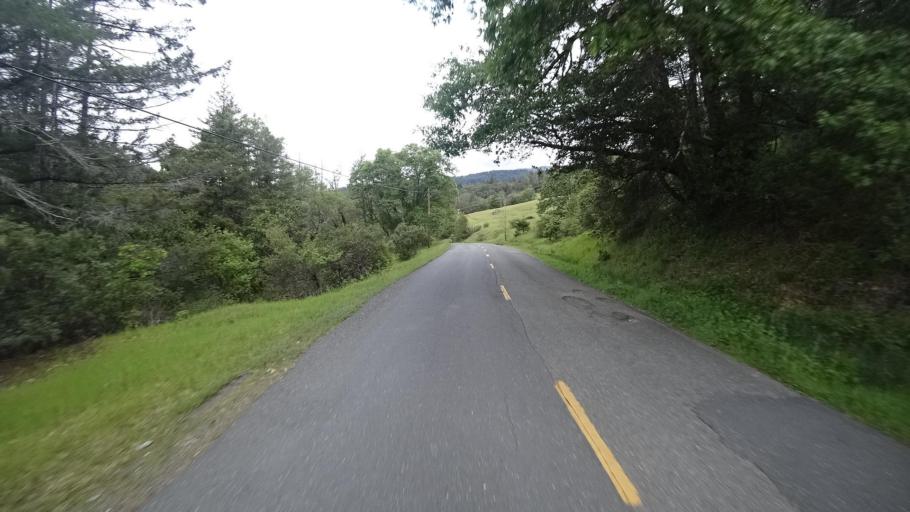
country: US
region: California
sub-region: Humboldt County
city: Redway
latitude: 40.2125
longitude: -123.5957
